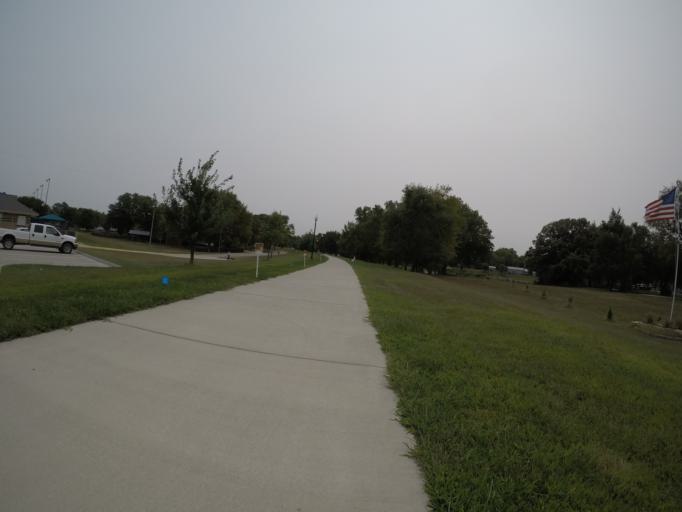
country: US
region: Kansas
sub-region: Marshall County
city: Marysville
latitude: 39.8394
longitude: -96.6486
